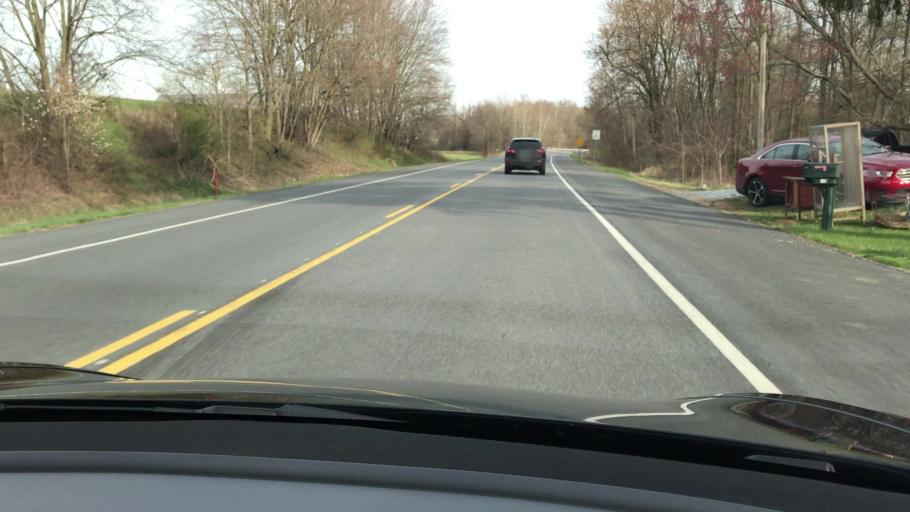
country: US
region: Pennsylvania
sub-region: York County
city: Valley Green
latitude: 40.1399
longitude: -76.8691
